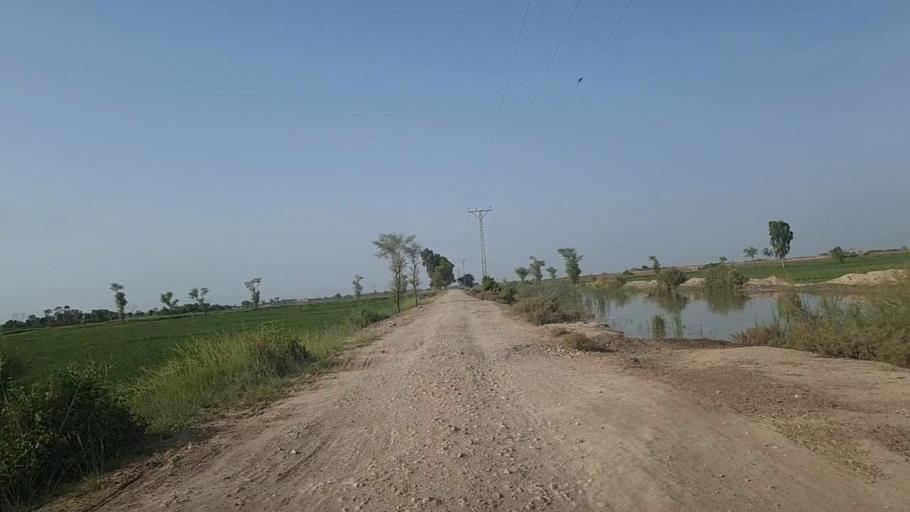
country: PK
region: Sindh
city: Sita Road
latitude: 27.1071
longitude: 67.8752
